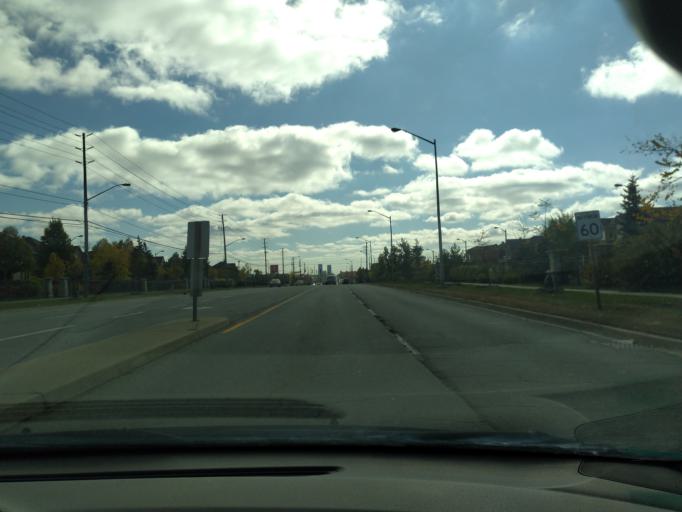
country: CA
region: Ontario
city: Vaughan
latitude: 43.8301
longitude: -79.5573
